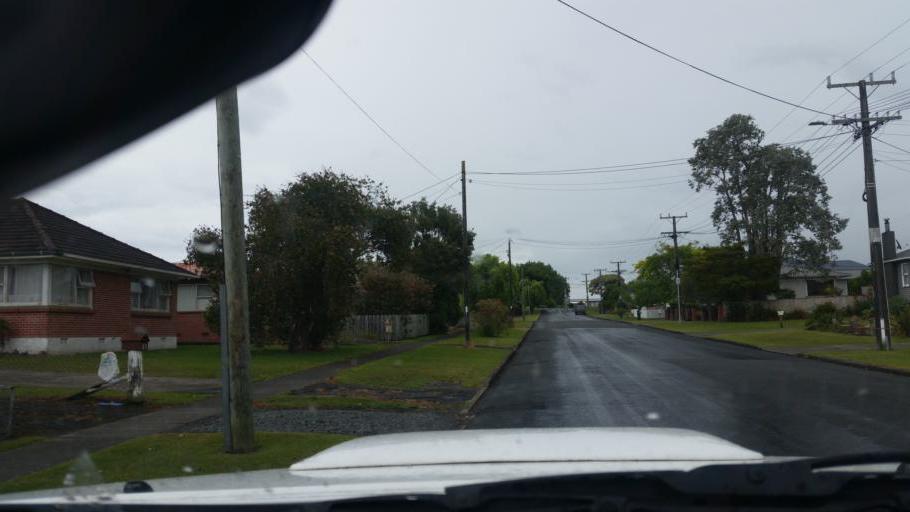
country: NZ
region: Northland
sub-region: Kaipara District
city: Dargaville
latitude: -35.9316
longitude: 173.8606
